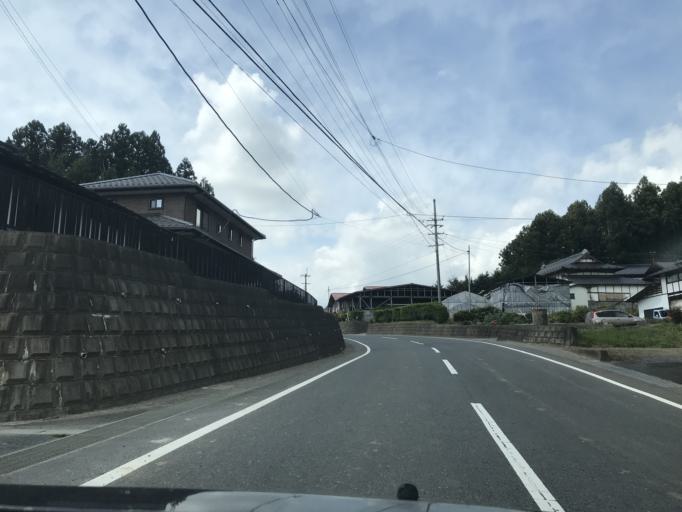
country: JP
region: Iwate
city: Ichinoseki
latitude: 38.7903
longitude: 141.0025
